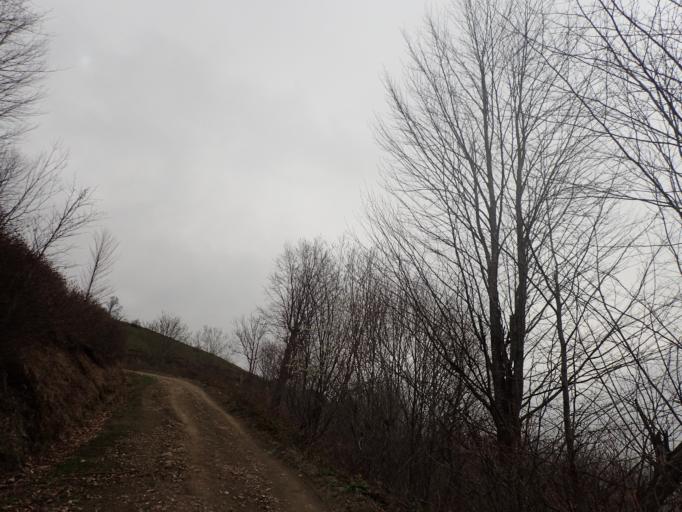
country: TR
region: Ordu
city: Kumru
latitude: 40.7809
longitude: 37.1864
